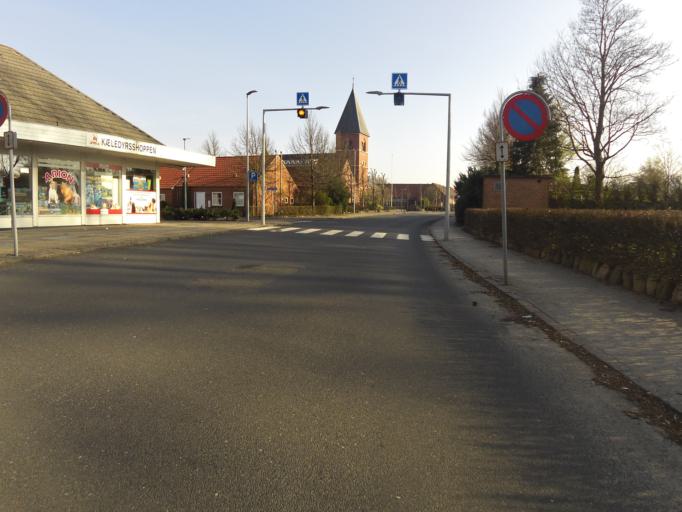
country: DK
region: South Denmark
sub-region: Vejen Kommune
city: Vejen
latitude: 55.4830
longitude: 9.1406
